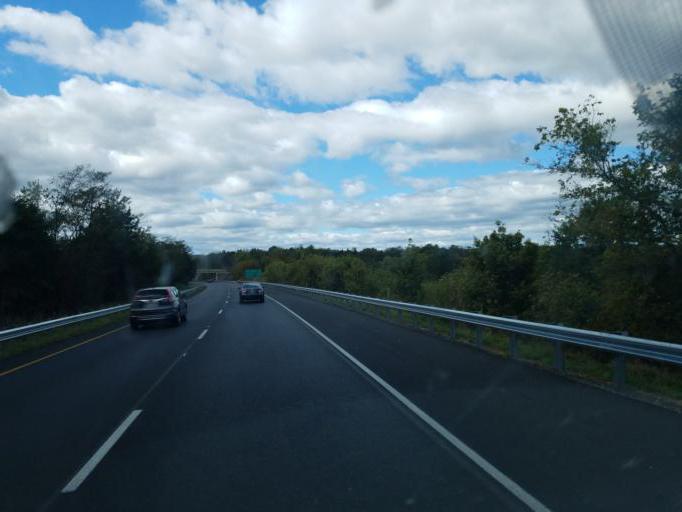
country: US
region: Maryland
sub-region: Washington County
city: Wilson-Conococheague
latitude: 39.6506
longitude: -77.8492
